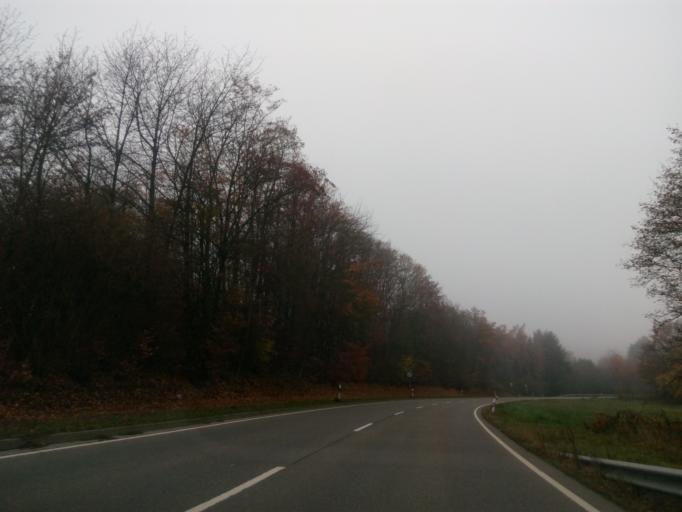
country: DE
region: Rheinland-Pfalz
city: Homberg
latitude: 49.6575
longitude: 7.5250
